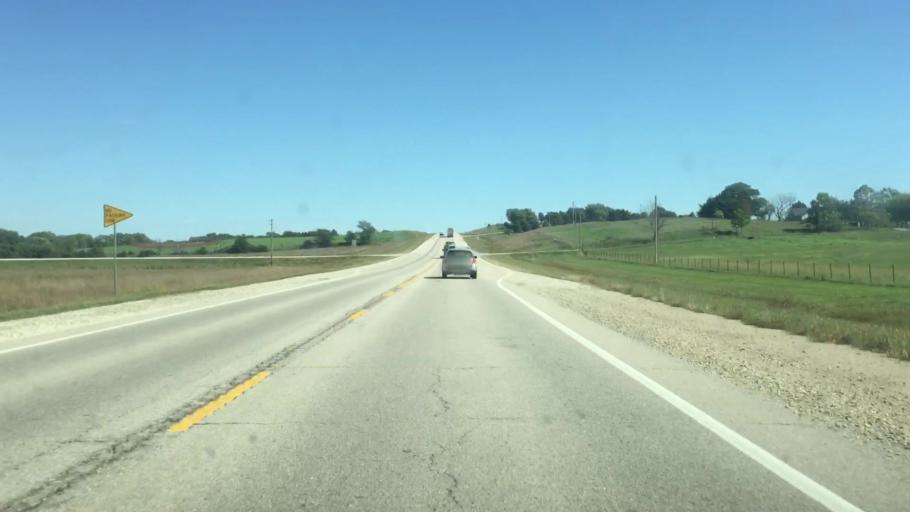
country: US
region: Kansas
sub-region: Nemaha County
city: Seneca
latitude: 39.8422
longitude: -95.9985
